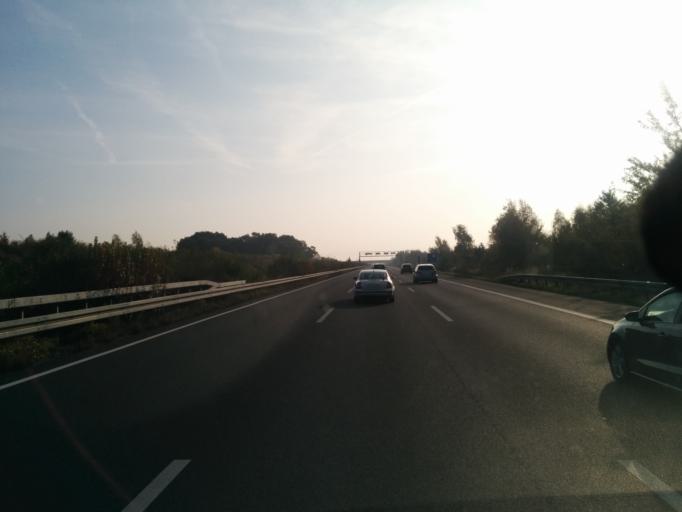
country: DE
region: Lower Saxony
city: Arpke
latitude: 52.3622
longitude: 10.1402
